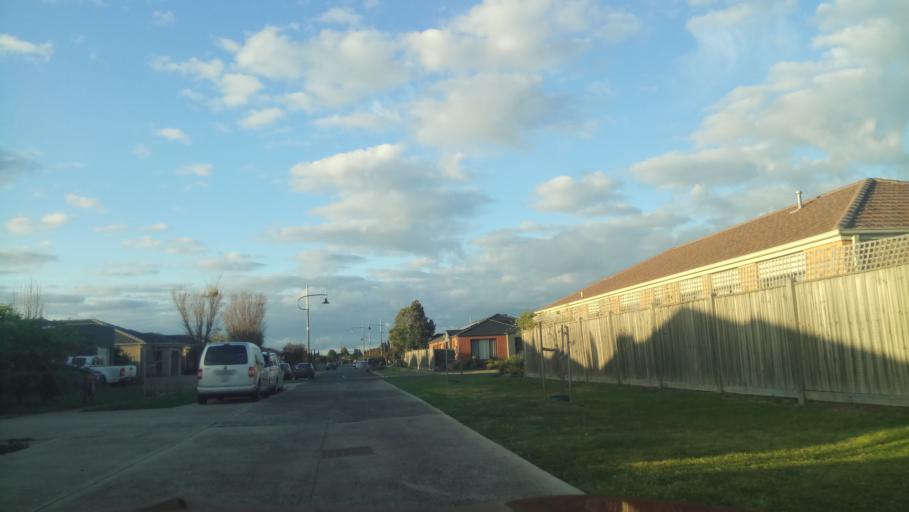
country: AU
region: Victoria
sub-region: Wyndham
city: Point Cook
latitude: -37.9095
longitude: 144.7351
